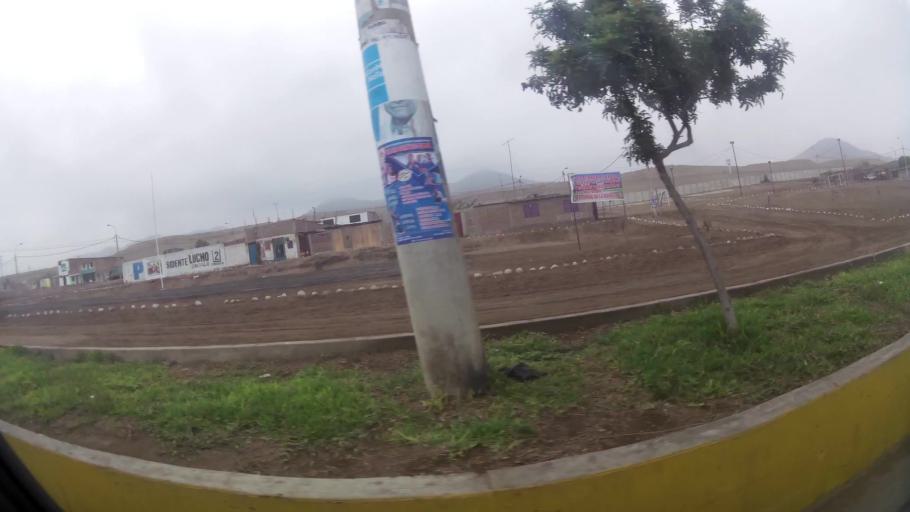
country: PE
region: Lima
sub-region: Provincia de Huaral
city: Chancay
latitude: -11.5874
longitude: -77.2580
